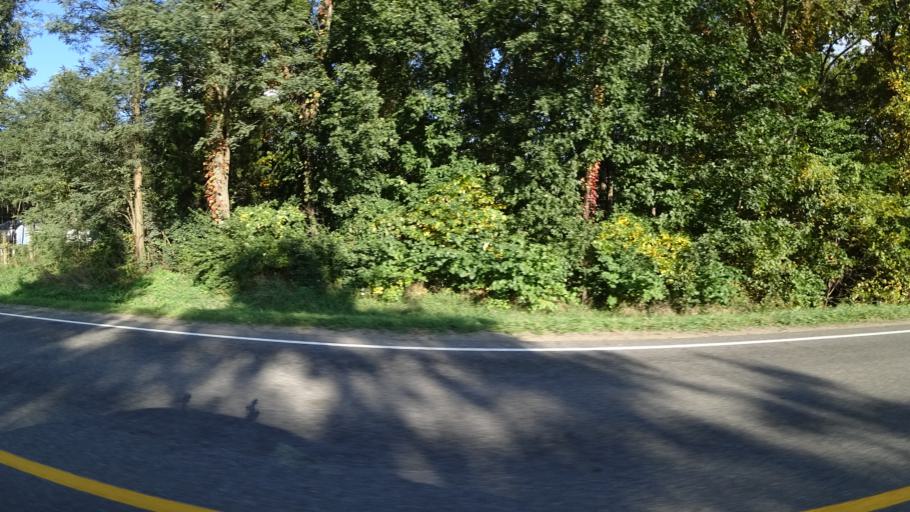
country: US
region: Michigan
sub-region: Saint Joseph County
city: Centreville
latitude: 41.8737
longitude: -85.5067
